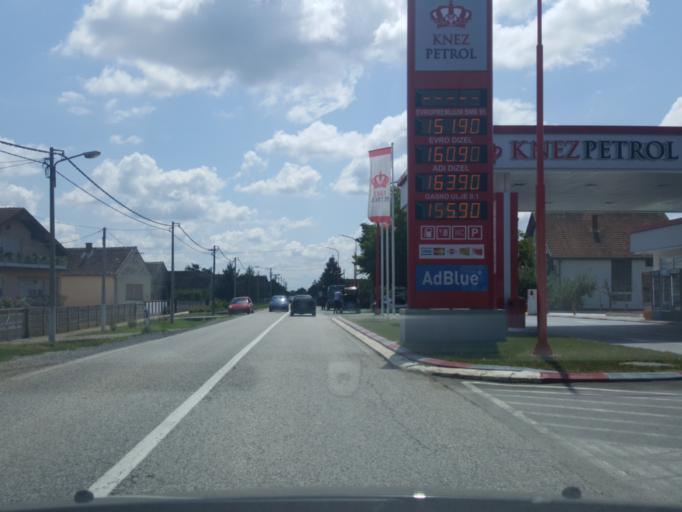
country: RS
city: Glusci
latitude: 44.8968
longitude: 19.5444
